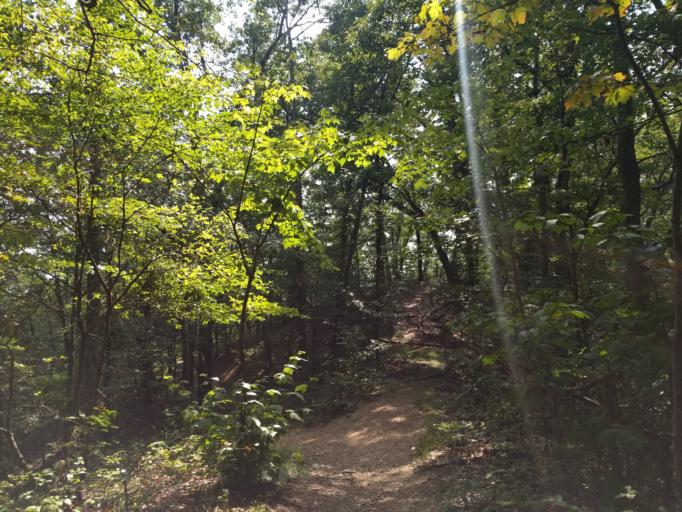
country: US
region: Virginia
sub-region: Smyth County
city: Marion
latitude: 36.8841
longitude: -81.5139
